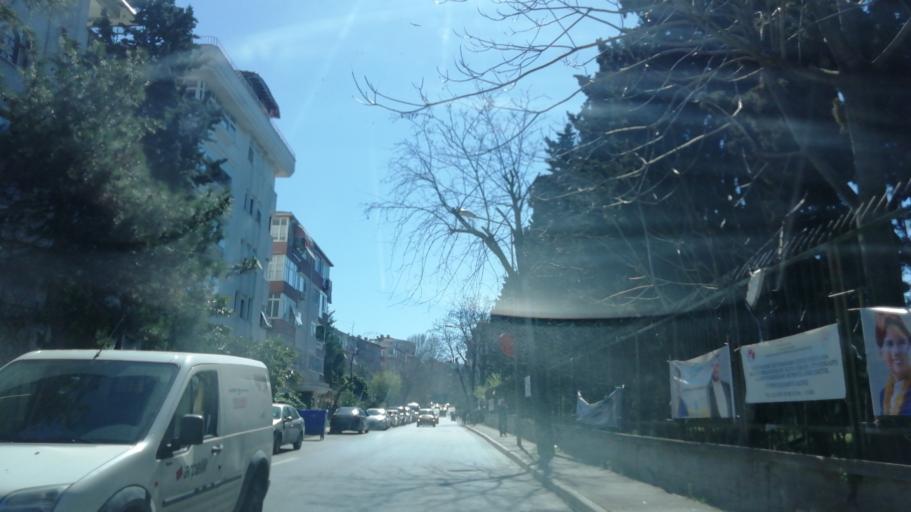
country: TR
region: Istanbul
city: Bahcelievler
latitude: 40.9853
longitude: 28.8667
